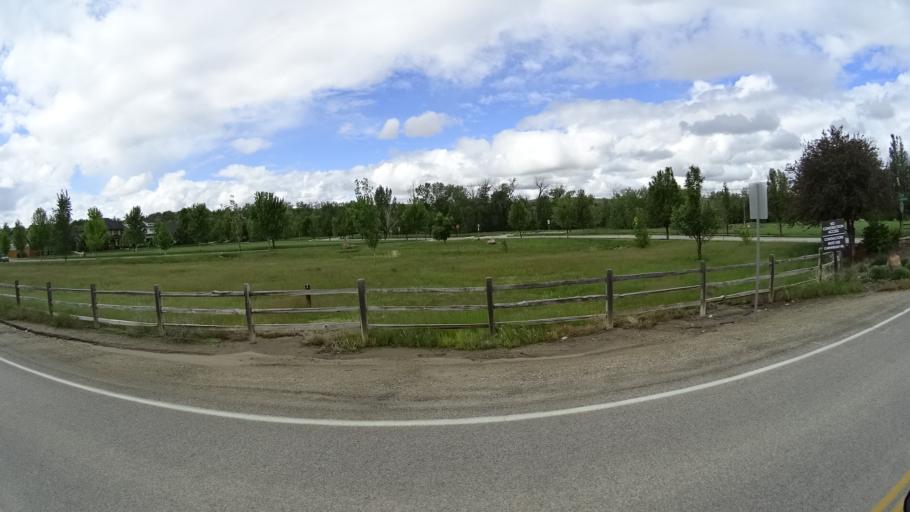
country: US
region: Idaho
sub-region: Ada County
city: Garden City
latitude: 43.7238
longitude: -116.2448
